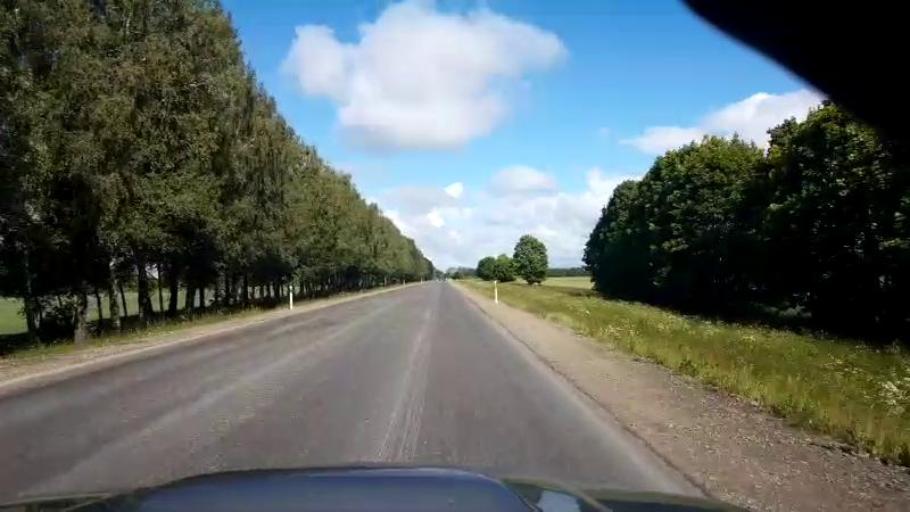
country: LV
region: Bauskas Rajons
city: Bauska
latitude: 56.3914
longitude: 24.2461
